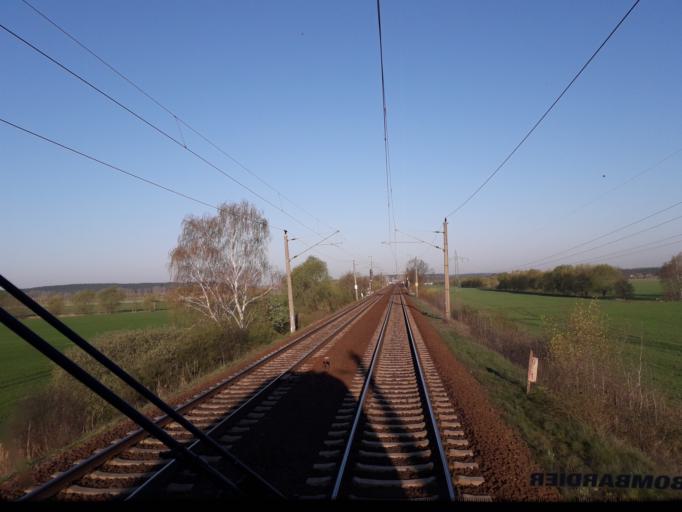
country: DE
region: Brandenburg
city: Stahnsdorf
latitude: 52.3217
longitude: 13.1584
